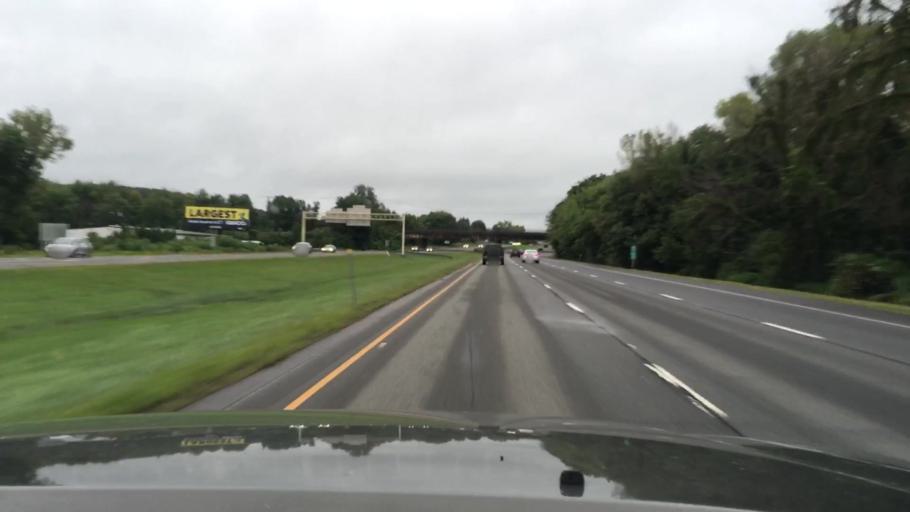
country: US
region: Connecticut
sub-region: New Haven County
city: Meriden
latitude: 41.5143
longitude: -72.7703
